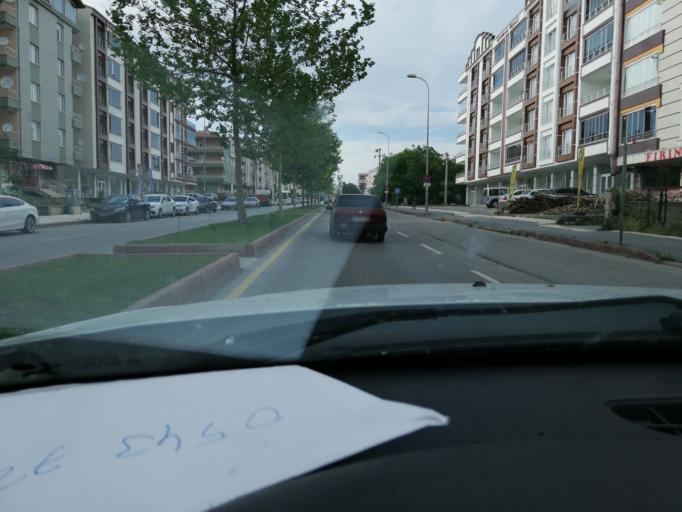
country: TR
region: Kirsehir
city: Kirsehir
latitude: 39.1333
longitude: 34.1592
